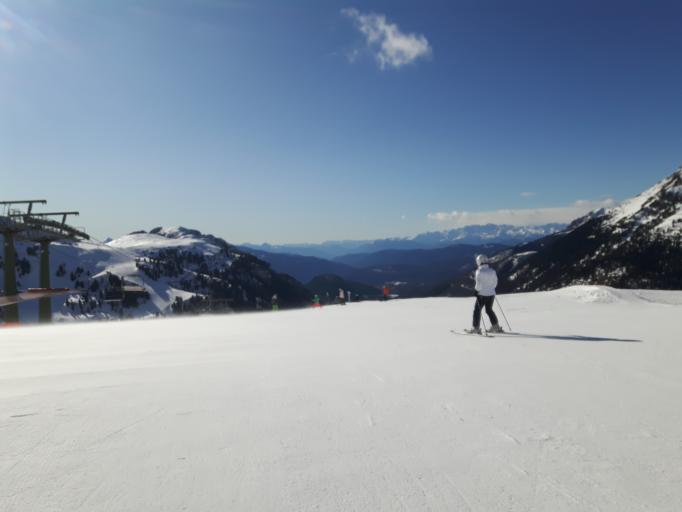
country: IT
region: Trentino-Alto Adige
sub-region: Provincia di Trento
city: Predazzo
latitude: 46.3469
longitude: 11.5584
